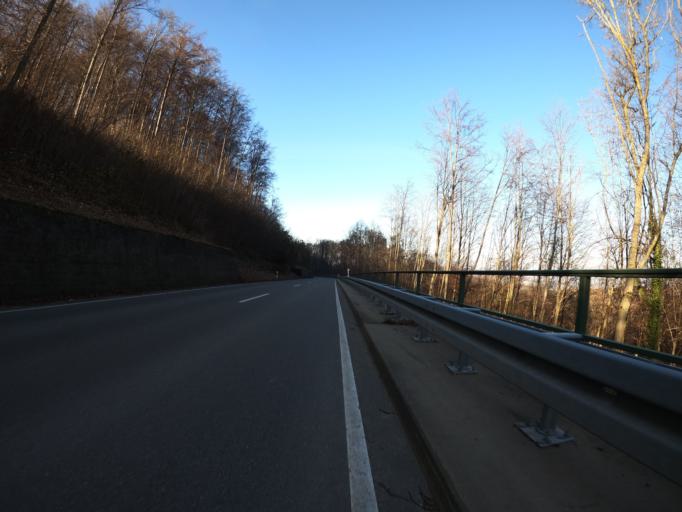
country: DE
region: Baden-Wuerttemberg
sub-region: Regierungsbezirk Stuttgart
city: Eschenbach
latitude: 48.6279
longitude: 9.6731
